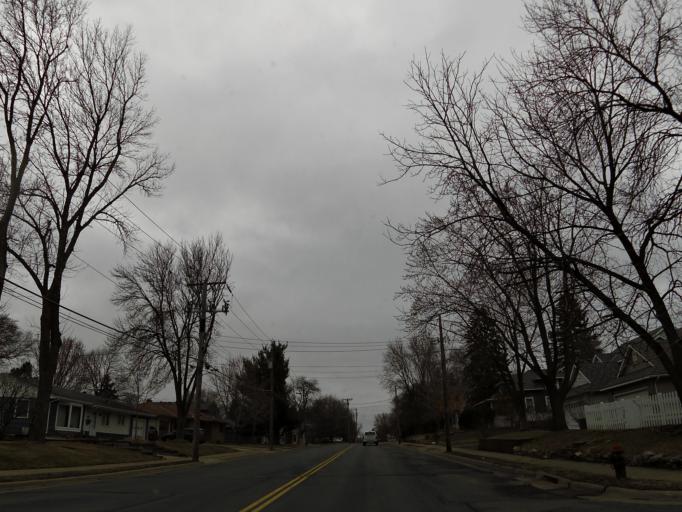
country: US
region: Minnesota
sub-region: Washington County
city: Stillwater
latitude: 45.0491
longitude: -92.8192
